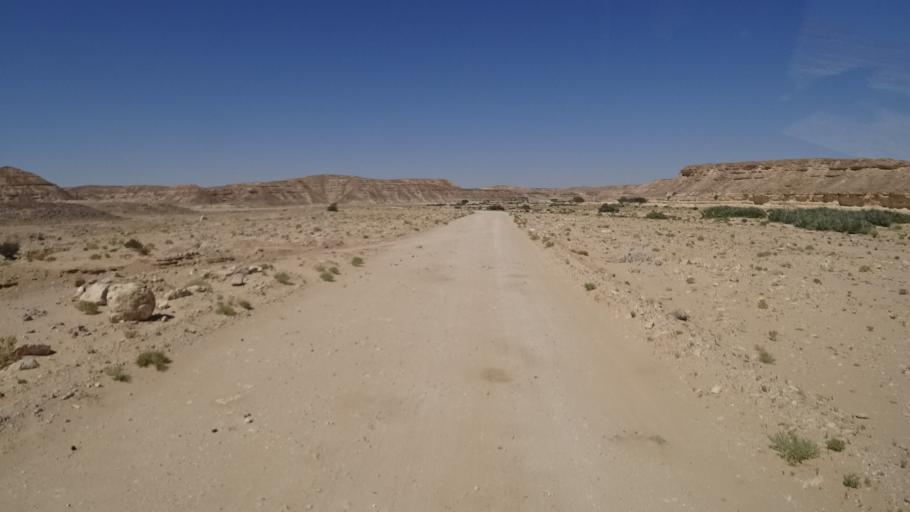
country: OM
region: Zufar
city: Salalah
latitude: 17.5012
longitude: 53.3651
